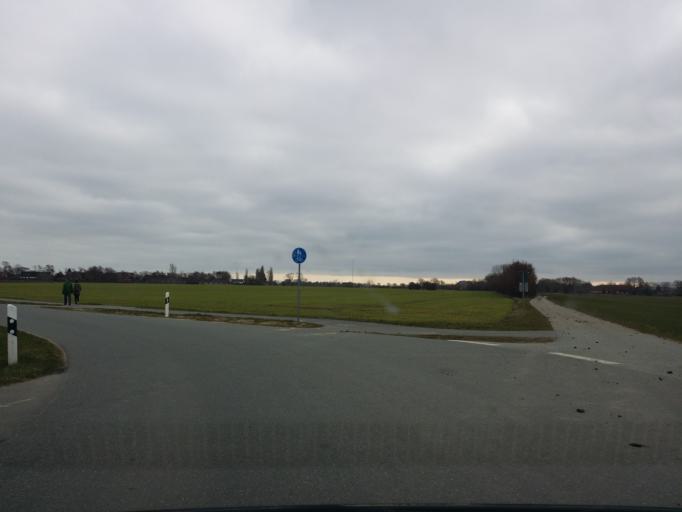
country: DE
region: Schleswig-Holstein
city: Grossenbrode
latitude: 54.4836
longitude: 11.0553
